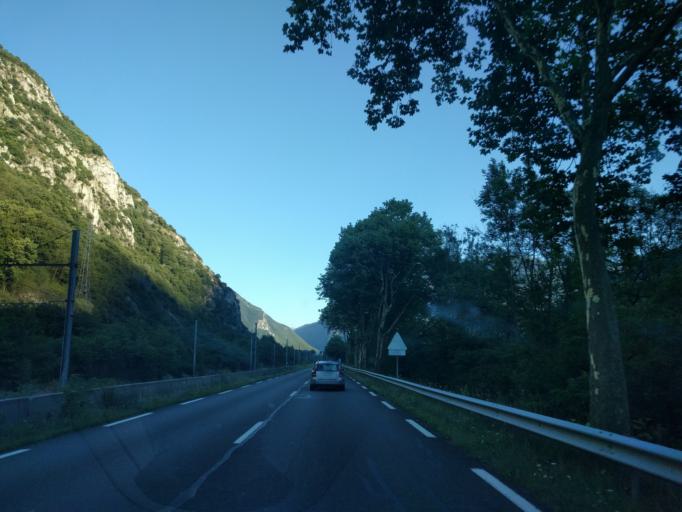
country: FR
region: Rhone-Alpes
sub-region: Departement de la Savoie
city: Saint-Etienne-de-Cuines
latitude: 45.3765
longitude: 6.2827
